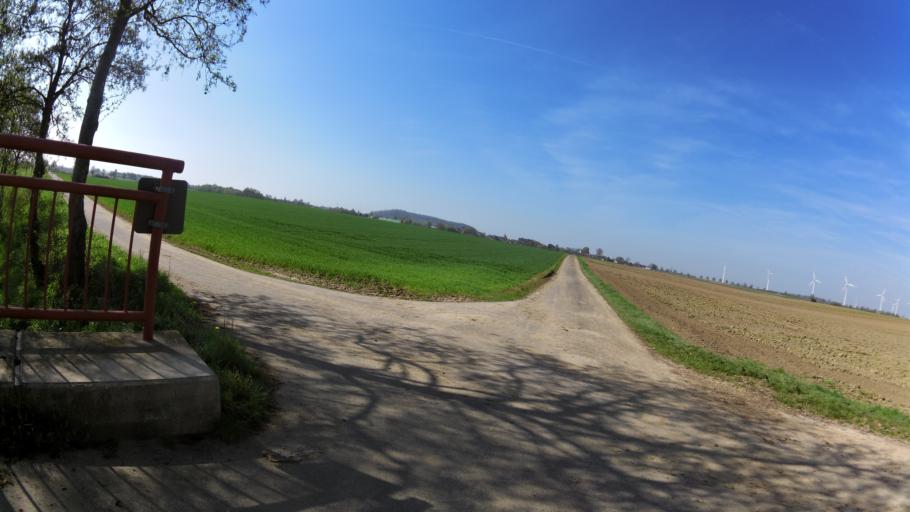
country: DE
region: North Rhine-Westphalia
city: Baesweiler
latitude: 50.9342
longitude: 6.1764
